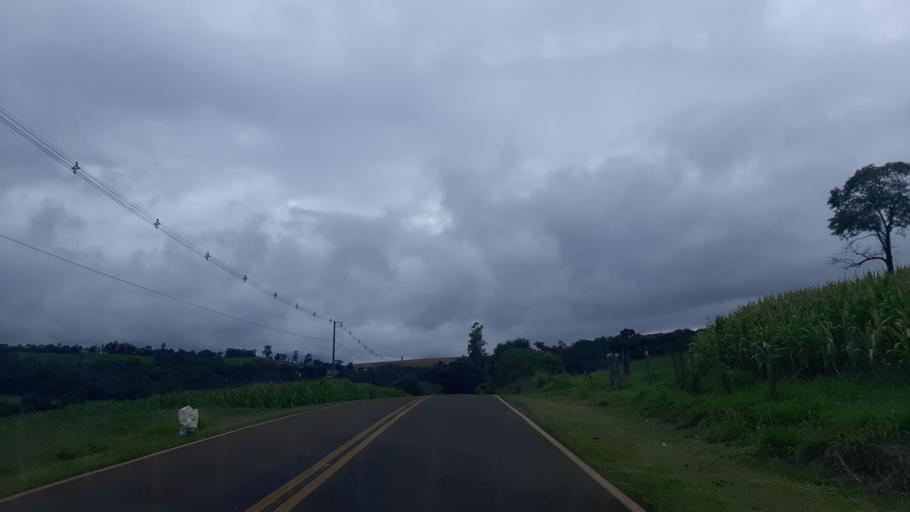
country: BR
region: Parana
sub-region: Ampere
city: Ampere
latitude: -25.9345
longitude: -53.4646
